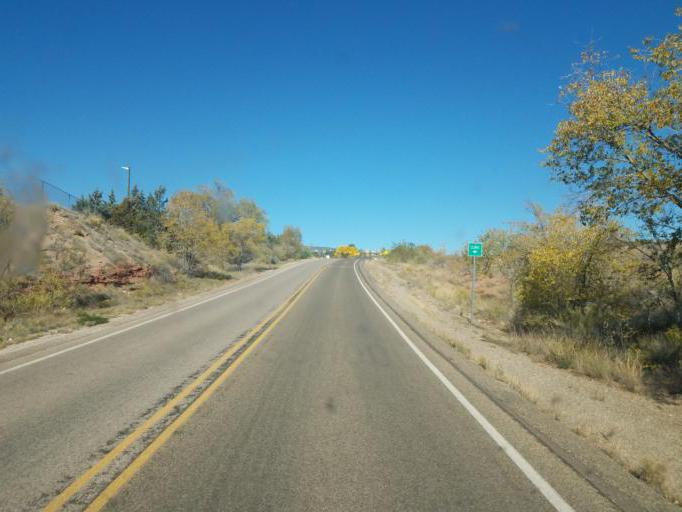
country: US
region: New Mexico
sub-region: Sandoval County
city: Jemez Pueblo
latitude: 35.6545
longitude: -106.7344
